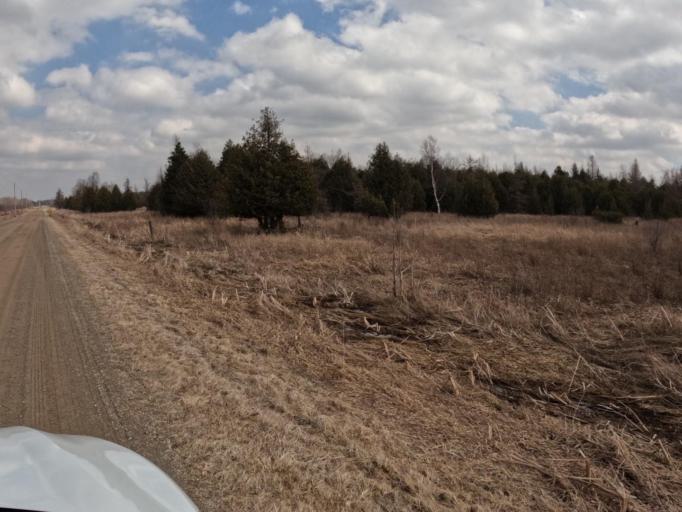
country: CA
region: Ontario
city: Shelburne
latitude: 44.0180
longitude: -80.3095
